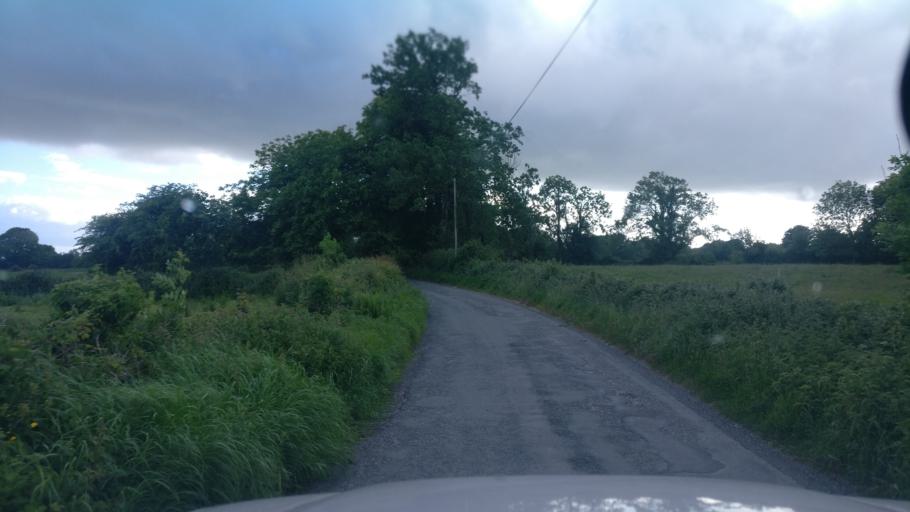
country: IE
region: Connaught
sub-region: County Galway
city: Ballinasloe
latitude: 53.2342
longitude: -8.2026
